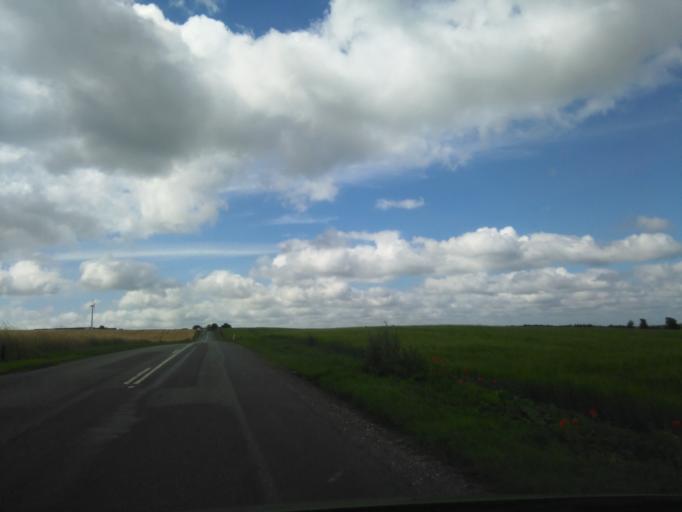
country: DK
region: Central Jutland
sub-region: Syddjurs Kommune
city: Ronde
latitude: 56.2587
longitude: 10.5081
